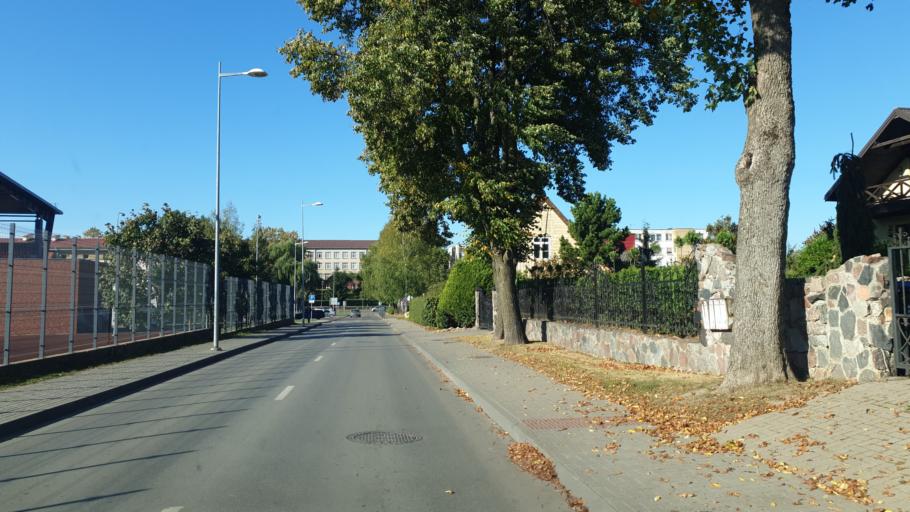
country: LT
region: Telsiu apskritis
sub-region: Telsiai
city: Telsiai
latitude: 55.9856
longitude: 22.2431
